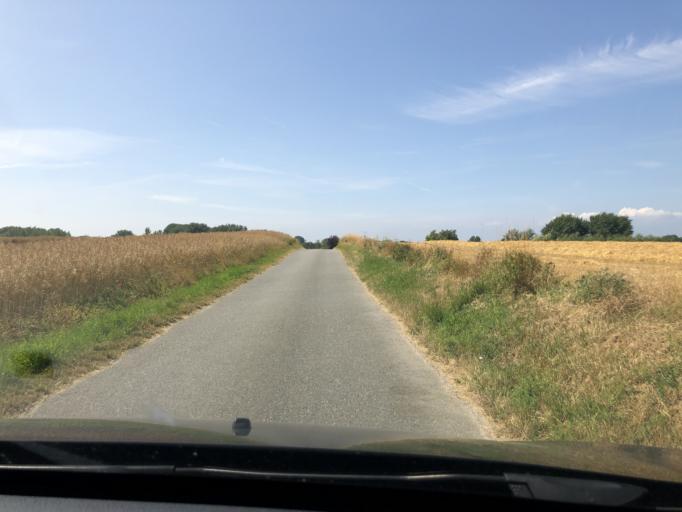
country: DK
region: South Denmark
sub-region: AEro Kommune
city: AEroskobing
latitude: 54.9193
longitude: 10.2969
